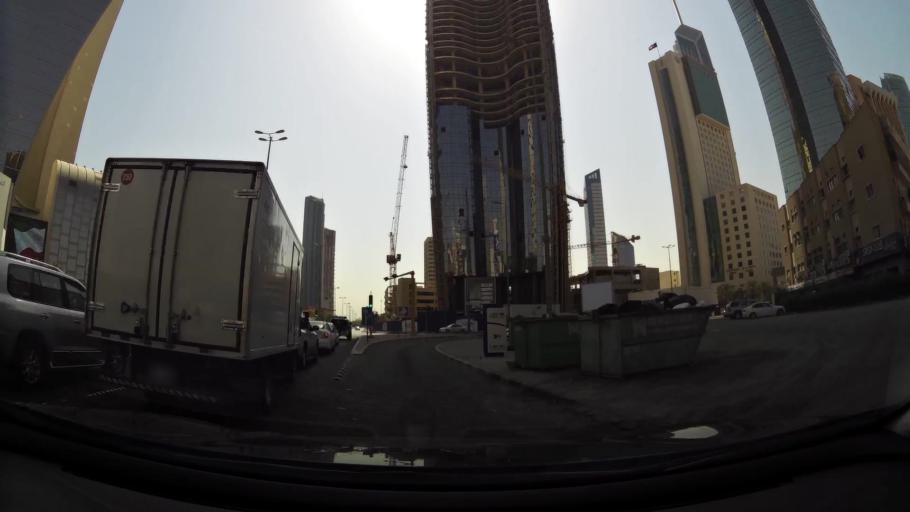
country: KW
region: Al Asimah
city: Kuwait City
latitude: 29.3795
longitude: 47.9915
